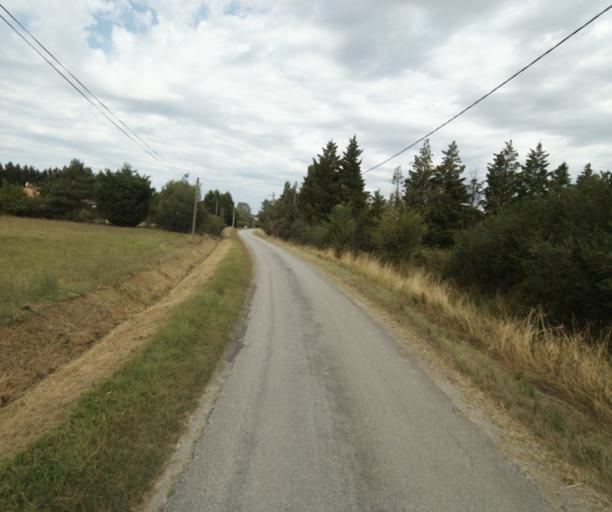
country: FR
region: Midi-Pyrenees
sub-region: Departement de la Haute-Garonne
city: Saint-Felix-Lauragais
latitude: 43.4315
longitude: 1.9430
